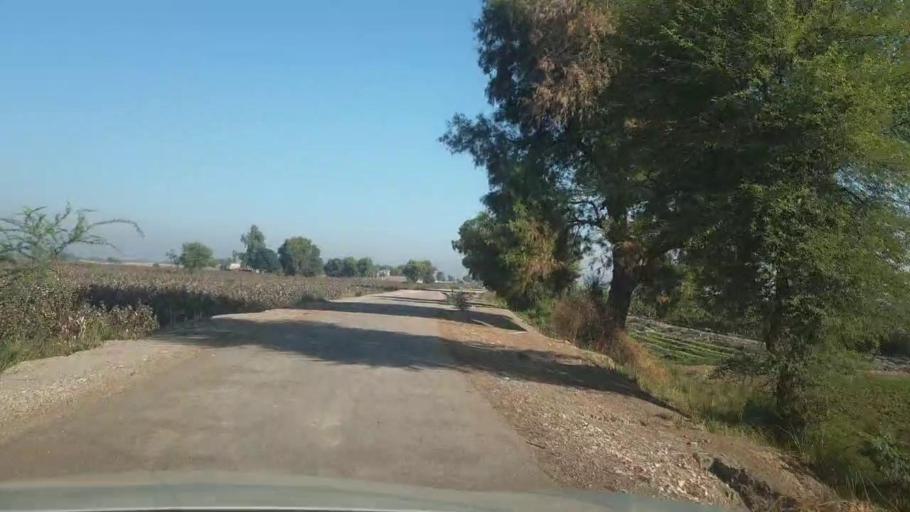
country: PK
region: Sindh
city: Bhan
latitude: 26.5420
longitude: 67.6888
